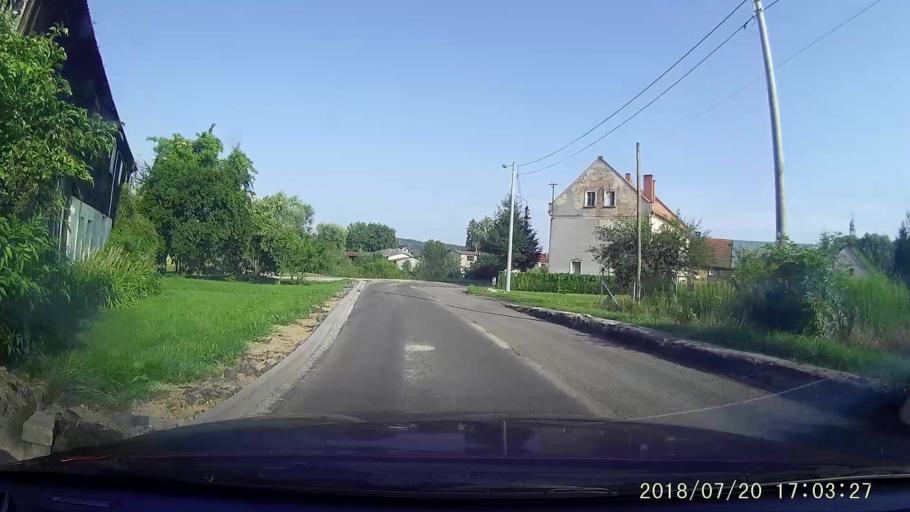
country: PL
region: Lower Silesian Voivodeship
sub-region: Powiat lubanski
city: Lesna
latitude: 51.0280
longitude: 15.2602
